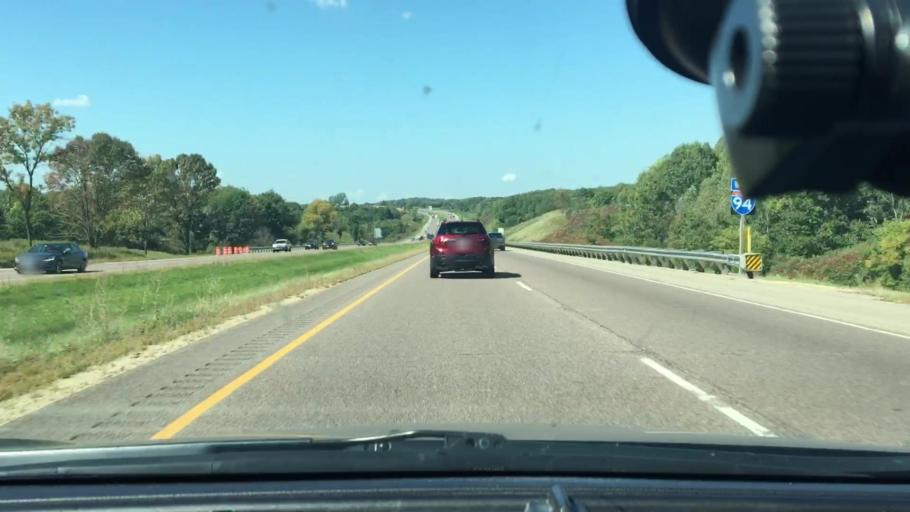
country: US
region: Wisconsin
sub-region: Pierce County
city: Spring Valley
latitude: 44.9228
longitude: -92.1250
